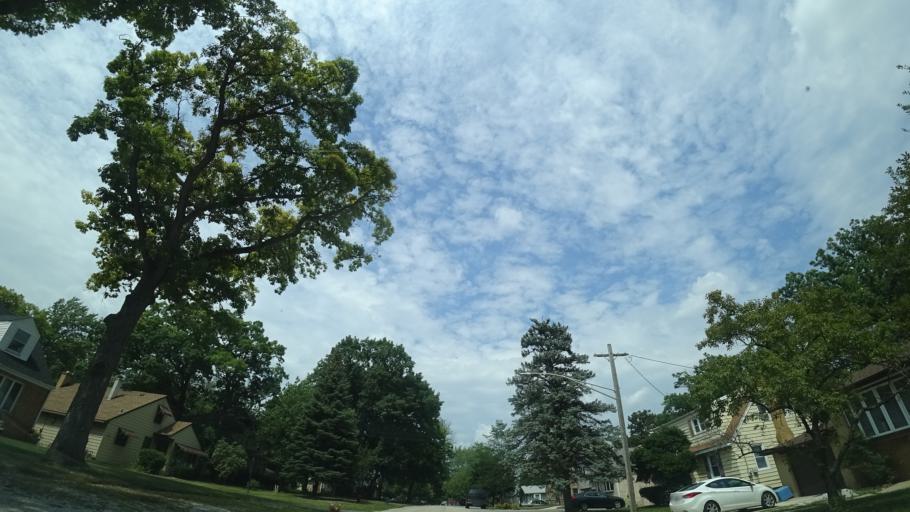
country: US
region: Illinois
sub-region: Cook County
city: Worth
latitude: 41.6875
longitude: -87.7936
